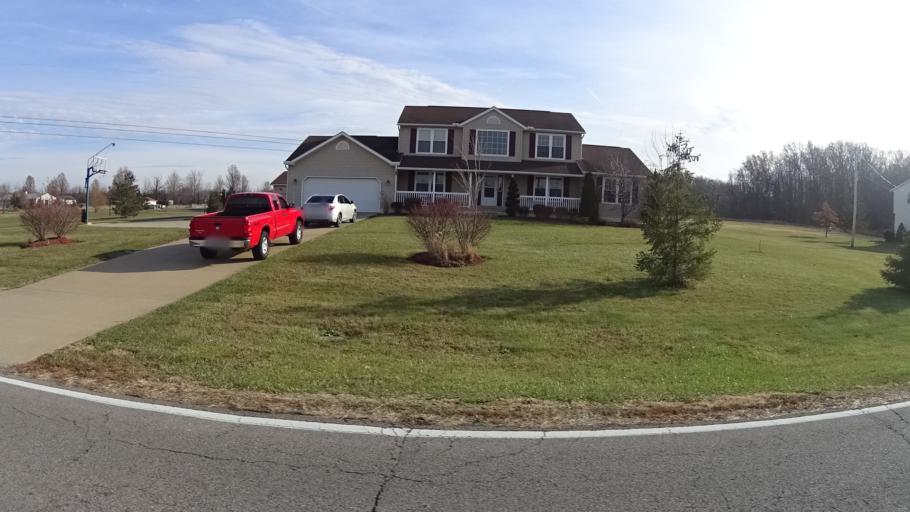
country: US
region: Ohio
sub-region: Lorain County
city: Grafton
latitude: 41.2344
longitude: -82.0426
